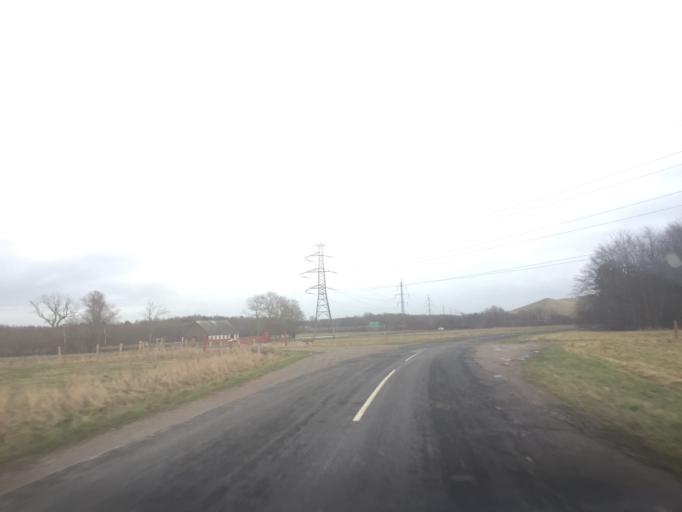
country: DK
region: Capital Region
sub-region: Albertslund Kommune
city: Albertslund
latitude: 55.6905
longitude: 12.3428
